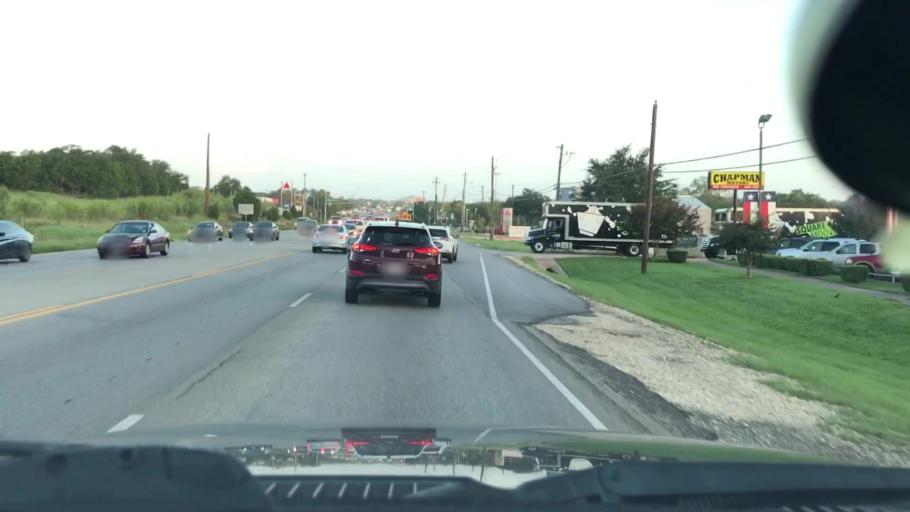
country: US
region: Texas
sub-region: Williamson County
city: Cedar Park
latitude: 30.4993
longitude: -97.8145
